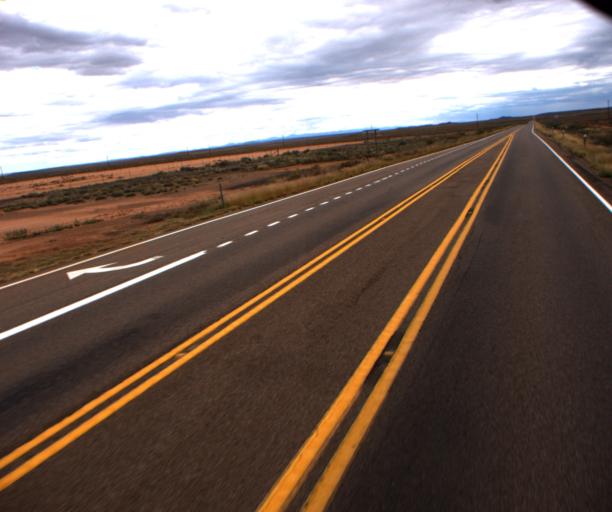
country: US
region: Arizona
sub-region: Navajo County
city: Holbrook
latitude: 34.7967
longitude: -110.1344
